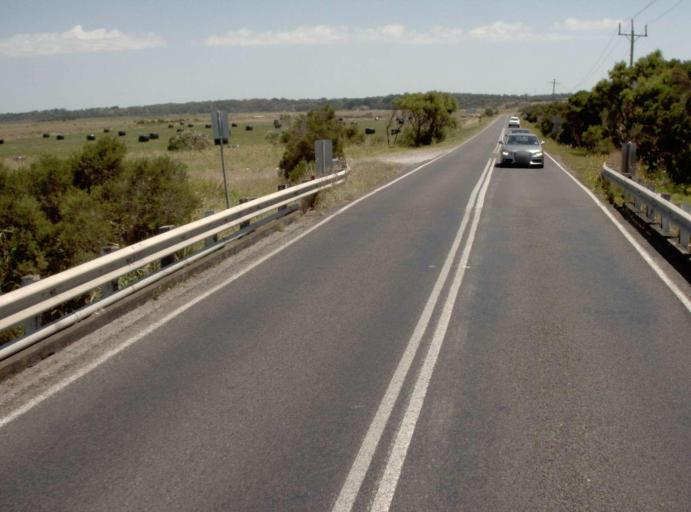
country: AU
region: Victoria
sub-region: Bass Coast
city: North Wonthaggi
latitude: -38.6946
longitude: 145.8777
